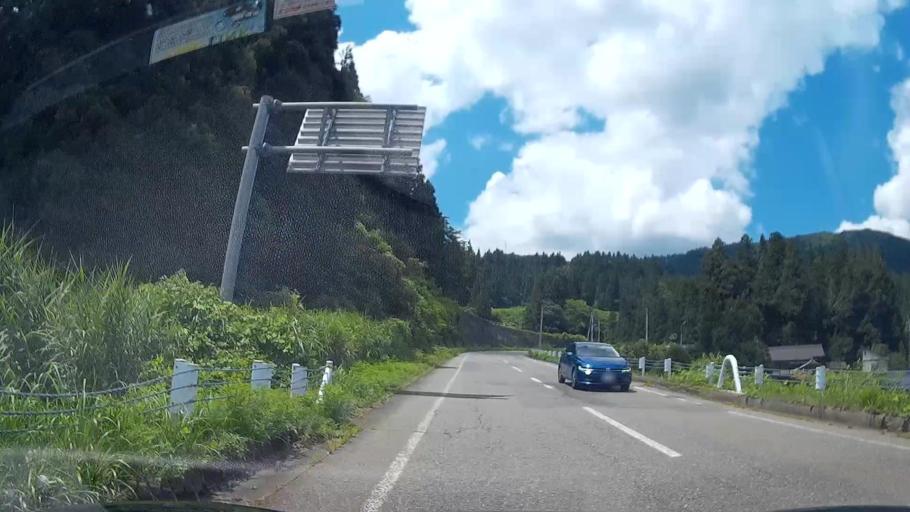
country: JP
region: Niigata
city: Shiozawa
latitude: 37.0224
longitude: 138.8053
